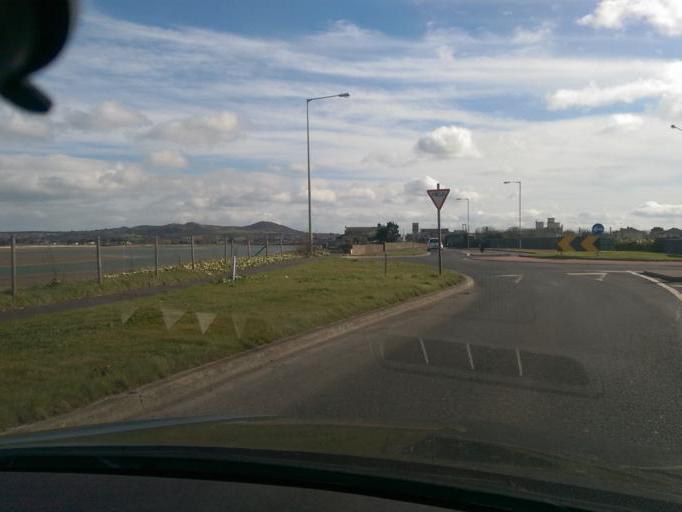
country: IE
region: Leinster
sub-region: Fingal County
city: Baldoyle
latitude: 53.4024
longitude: -6.1311
